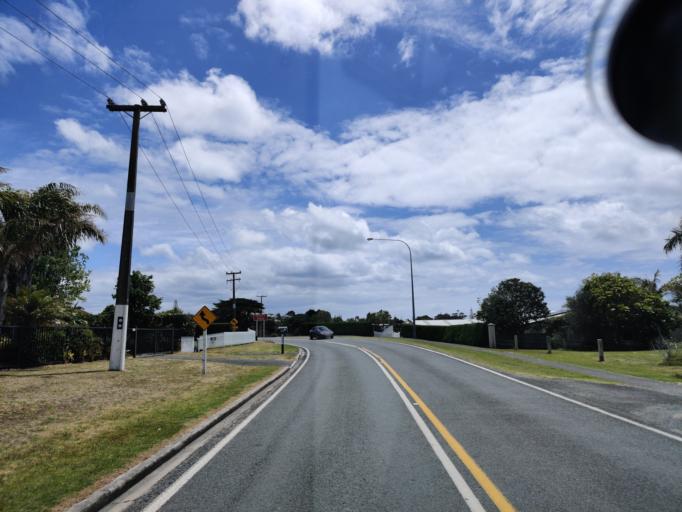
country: NZ
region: Northland
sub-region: Far North District
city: Kaitaia
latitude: -34.8139
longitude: 173.1178
